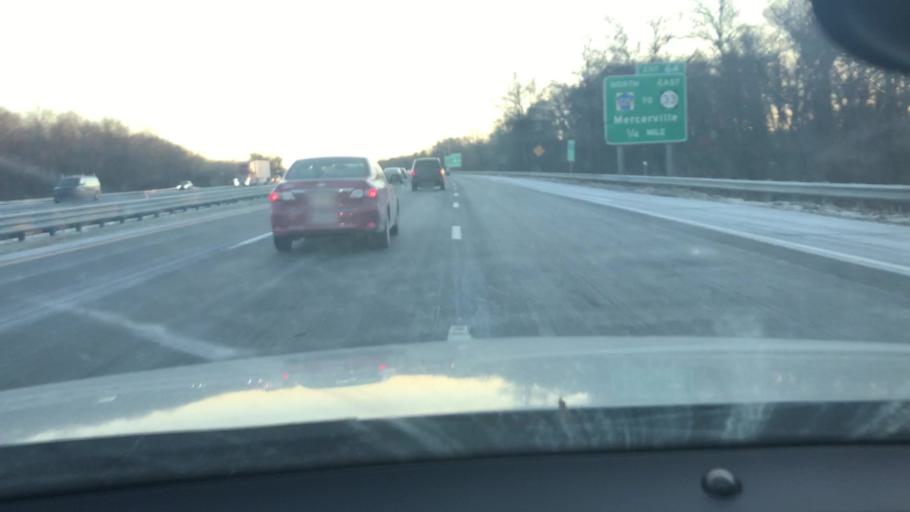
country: US
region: New Jersey
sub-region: Mercer County
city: Mercerville
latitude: 40.2456
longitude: -74.7002
